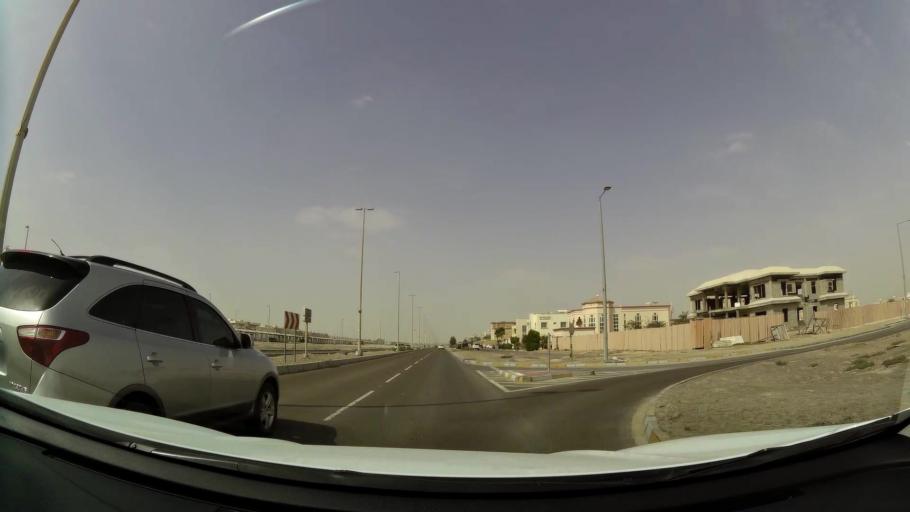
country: AE
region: Abu Dhabi
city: Abu Dhabi
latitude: 24.4104
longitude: 54.5503
